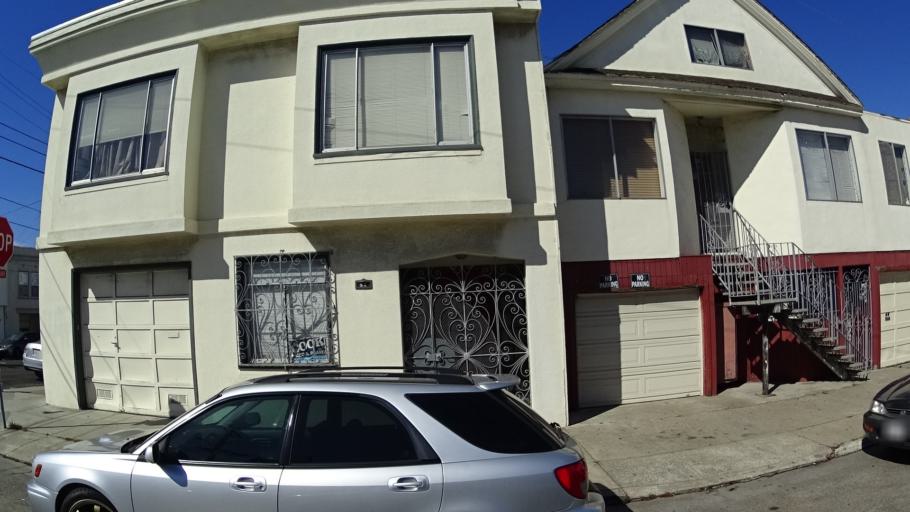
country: US
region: California
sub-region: San Francisco County
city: San Francisco
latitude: 37.7310
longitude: -122.4059
